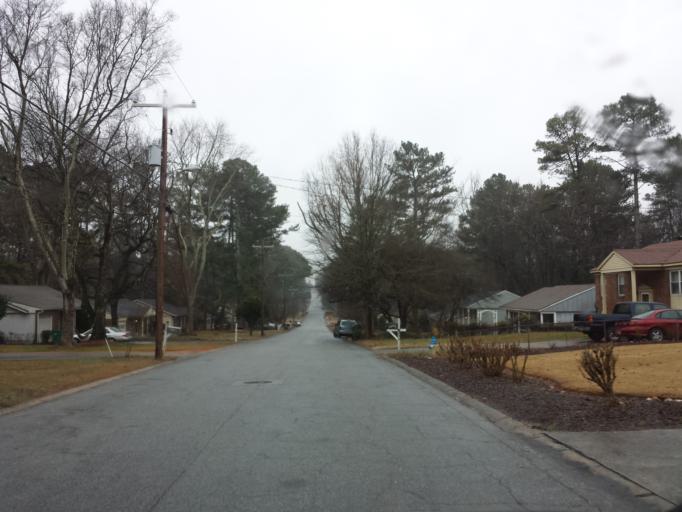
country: US
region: Georgia
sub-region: Cobb County
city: Smyrna
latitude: 33.8909
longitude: -84.4874
